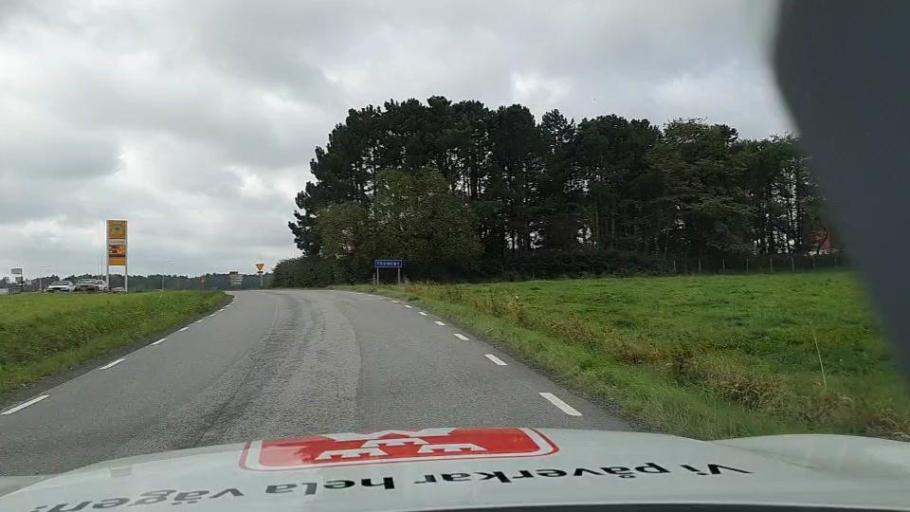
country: SE
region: Vaestra Goetaland
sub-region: Orust
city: Henan
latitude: 58.1520
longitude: 11.5902
